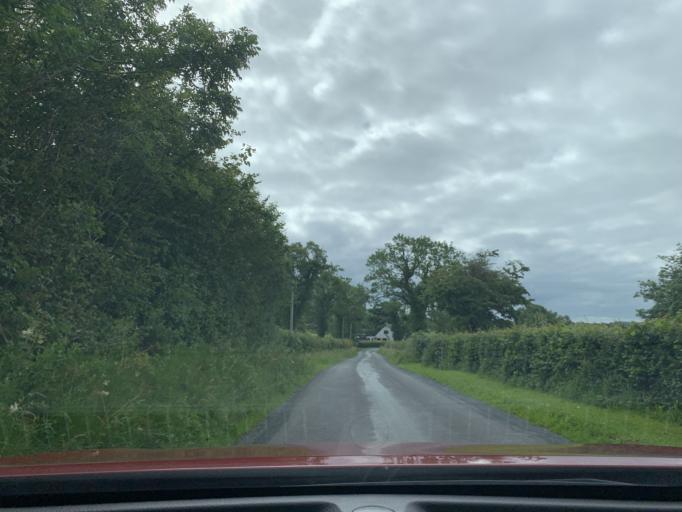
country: IE
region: Connaught
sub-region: Sligo
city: Sligo
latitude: 54.3382
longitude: -8.4762
